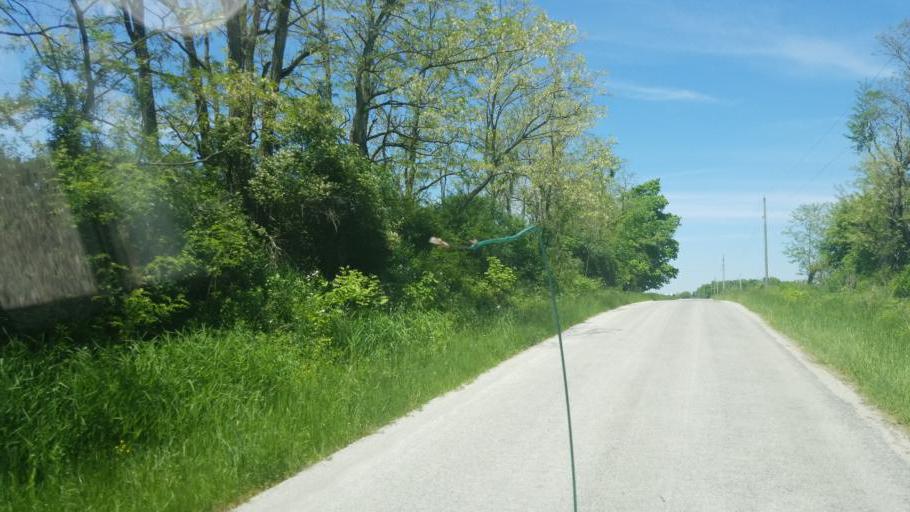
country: US
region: Ohio
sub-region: Huron County
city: New London
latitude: 41.0081
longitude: -82.4337
